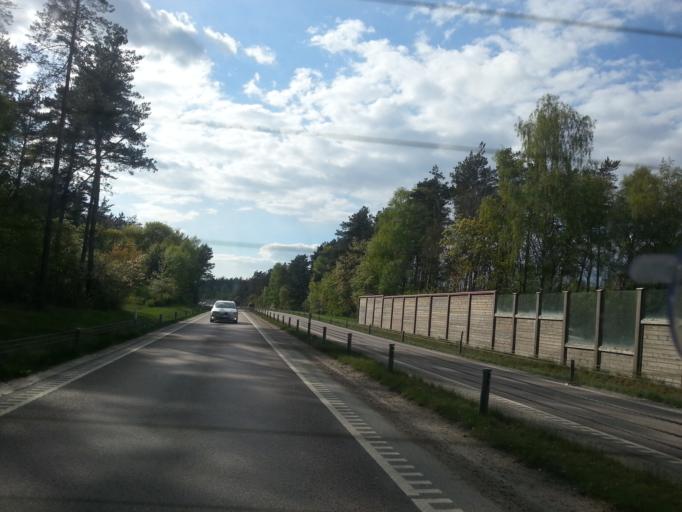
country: SE
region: Skane
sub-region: Sjobo Kommun
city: Sjoebo
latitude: 55.6357
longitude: 13.6703
